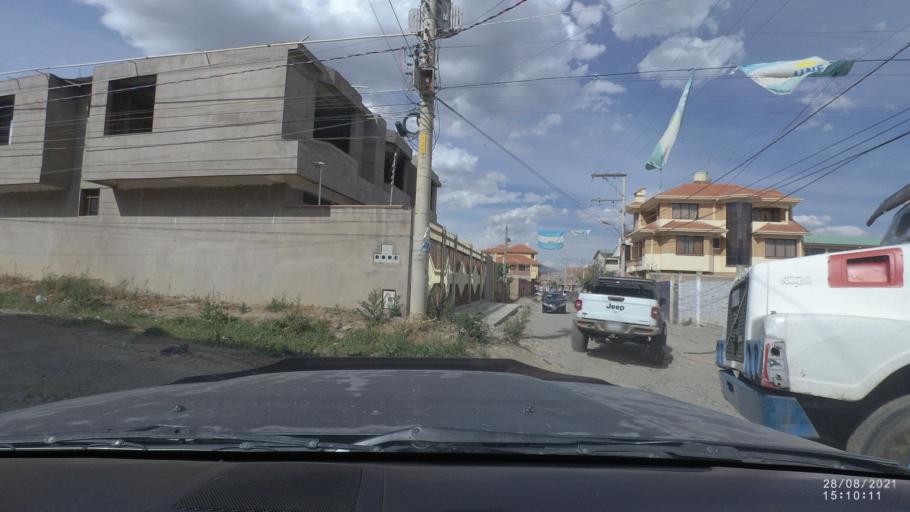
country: BO
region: Cochabamba
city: Cochabamba
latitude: -17.3384
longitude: -66.2688
